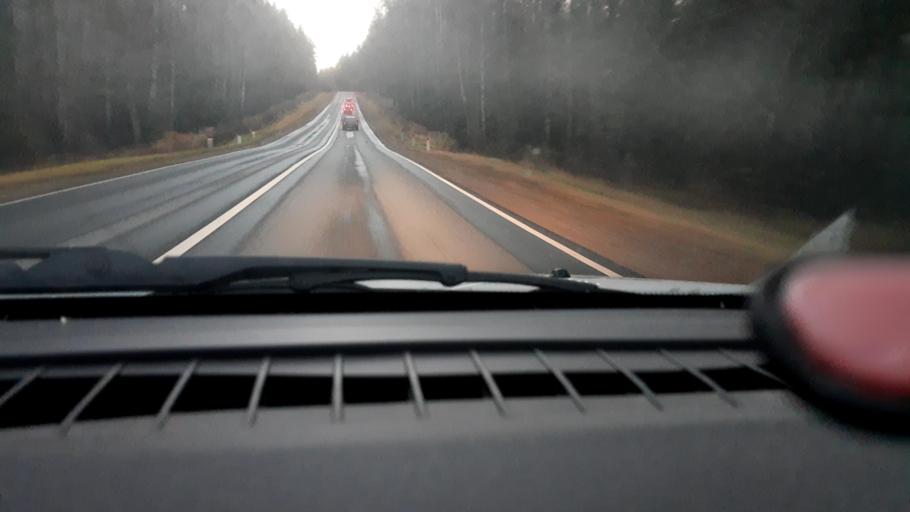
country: RU
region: Nizjnij Novgorod
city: Krasnyye Baki
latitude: 56.9964
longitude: 45.1138
